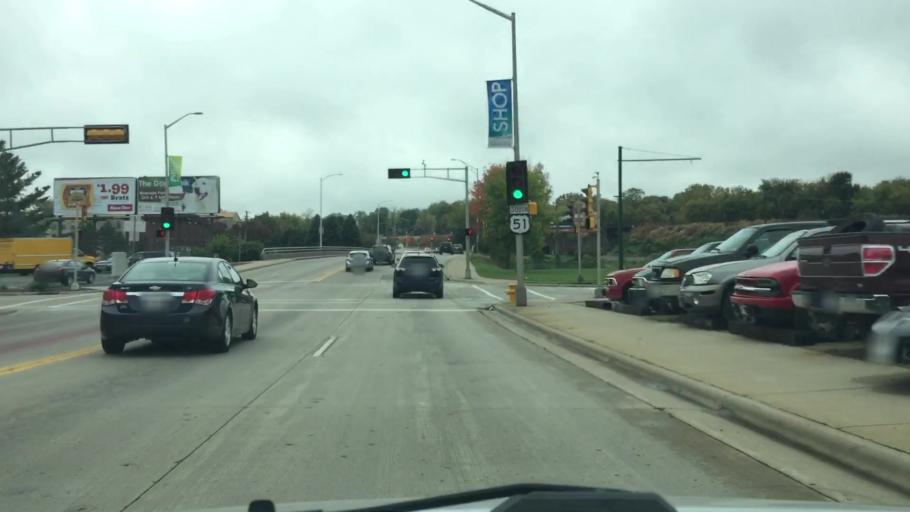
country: US
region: Wisconsin
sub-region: Rock County
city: Janesville
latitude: 42.6860
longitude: -89.0254
